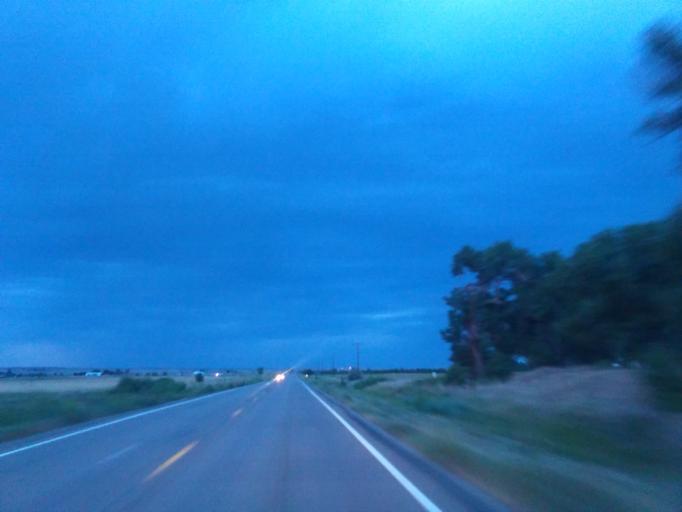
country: US
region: Colorado
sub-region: Las Animas County
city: Trinidad
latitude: 37.2670
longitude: -104.3518
